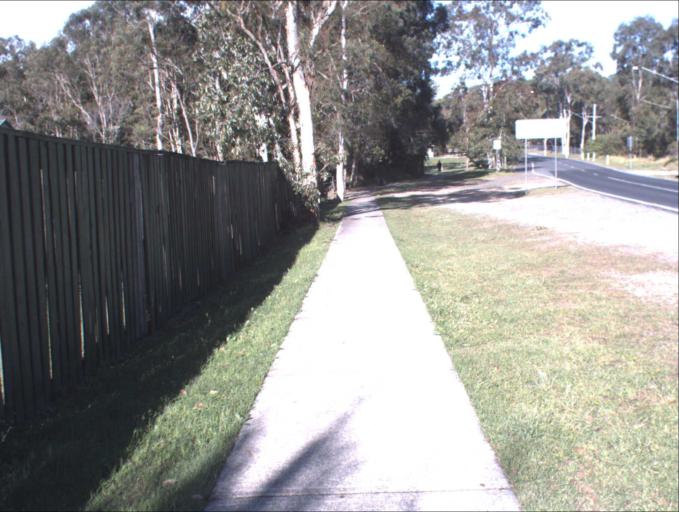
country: AU
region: Queensland
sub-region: Logan
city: Logan Reserve
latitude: -27.6982
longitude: 153.0872
